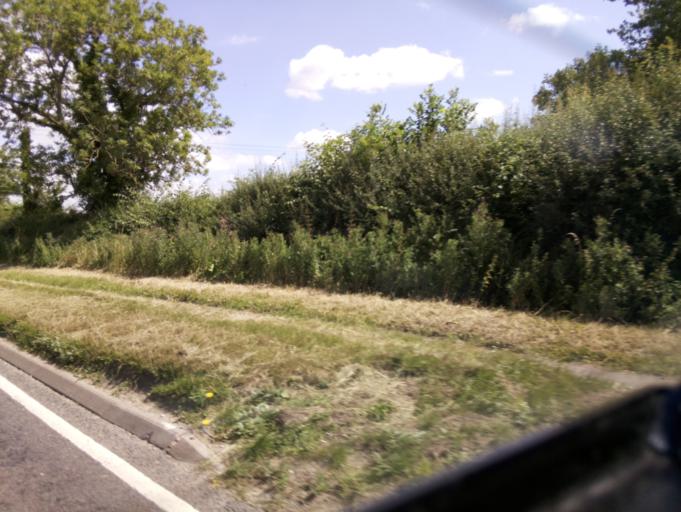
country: GB
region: England
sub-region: Buckinghamshire
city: Aylesbury
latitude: 51.8693
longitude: -0.8329
